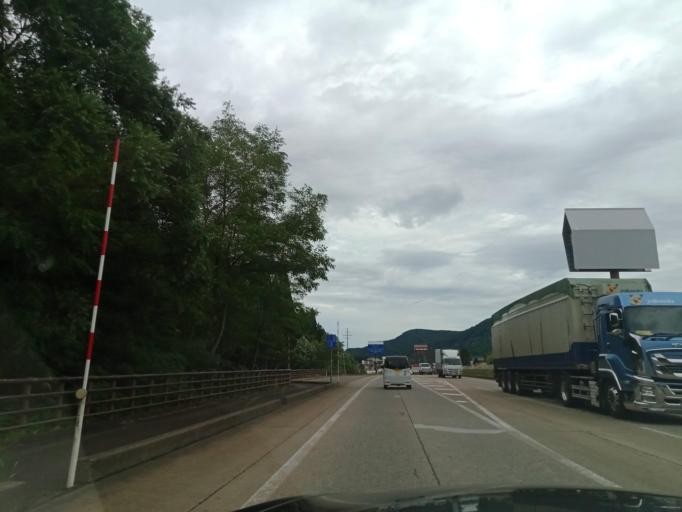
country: JP
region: Niigata
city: Arai
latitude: 36.8747
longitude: 138.2020
